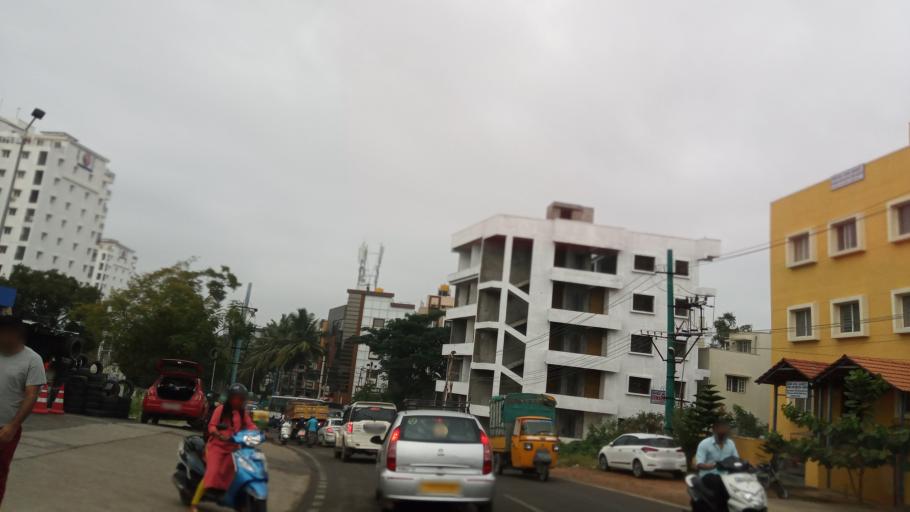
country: IN
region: Karnataka
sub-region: Bangalore Urban
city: Bangalore
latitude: 12.9051
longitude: 77.5291
